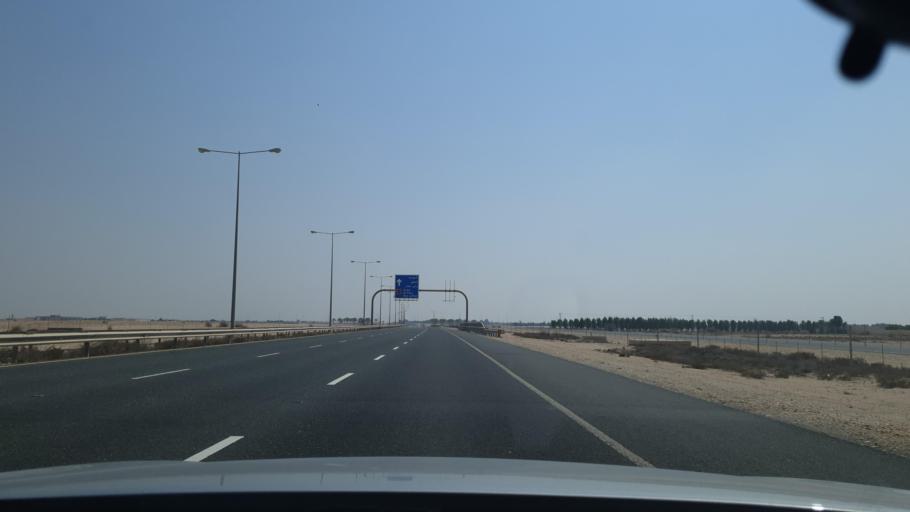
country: QA
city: Al Ghuwayriyah
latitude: 25.7930
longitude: 51.3891
